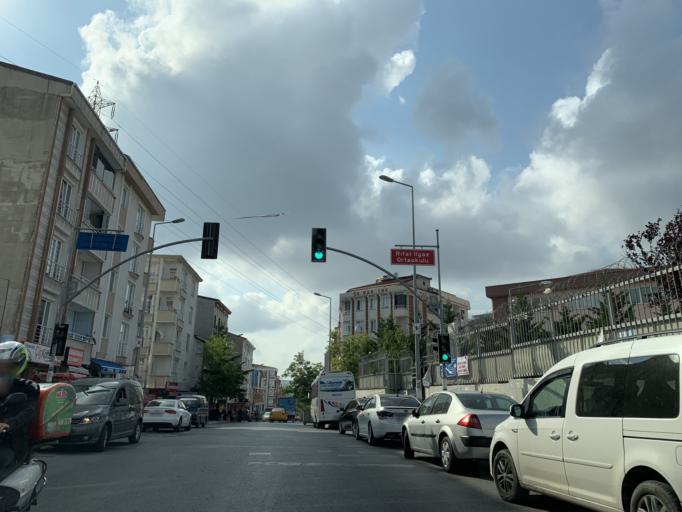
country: TR
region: Istanbul
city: Esenyurt
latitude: 41.0252
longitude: 28.6747
